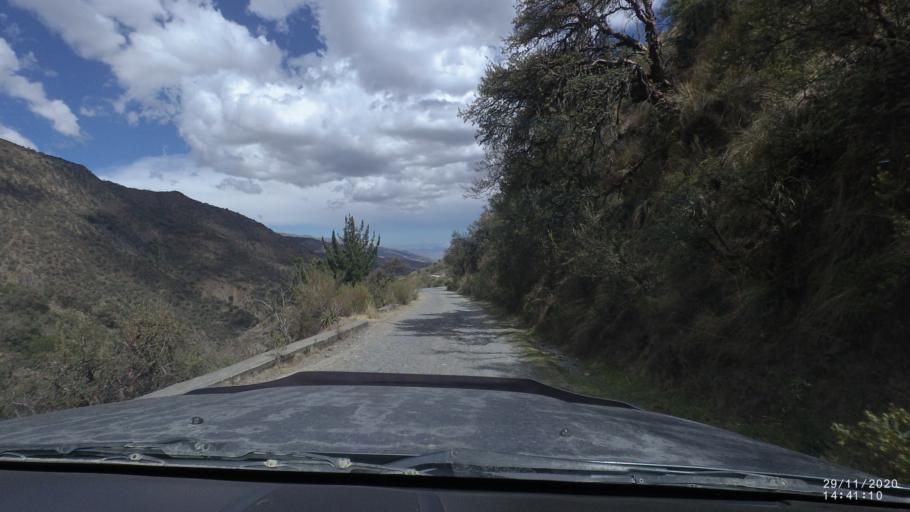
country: BO
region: Cochabamba
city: Sipe Sipe
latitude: -17.2768
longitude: -66.3265
